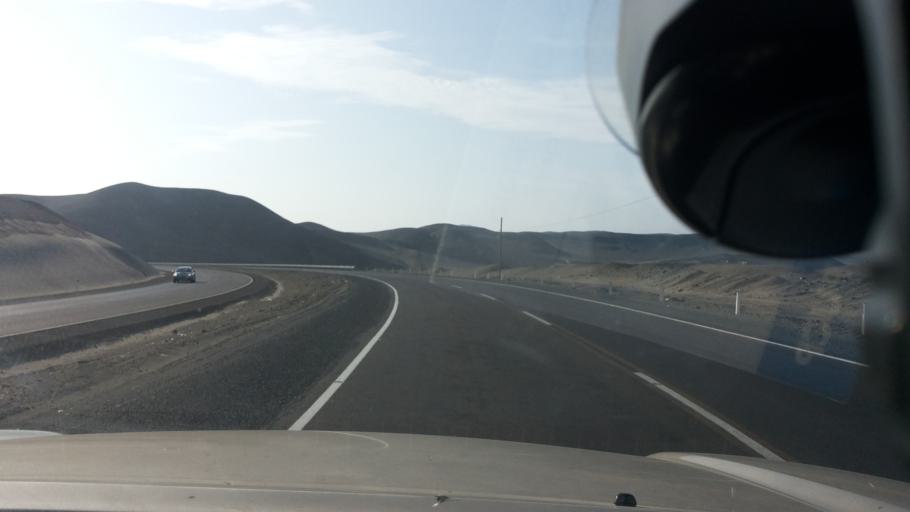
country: PE
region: Ancash
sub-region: Provincia de Huarmey
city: La Caleta Culebras
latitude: -9.7763
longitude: -78.2202
